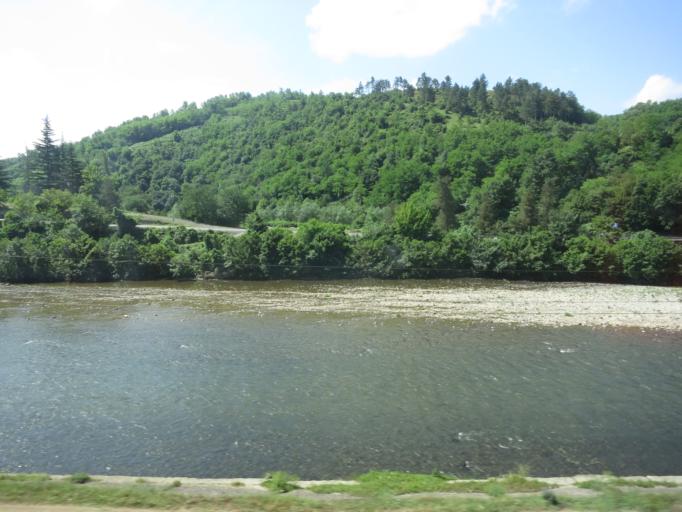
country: GE
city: Shorapani
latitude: 42.0946
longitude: 43.0904
